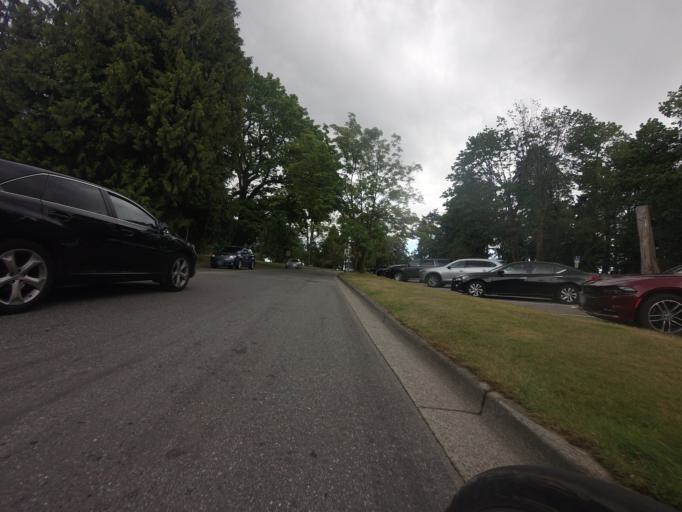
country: CA
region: British Columbia
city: West End
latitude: 49.2932
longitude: -123.1481
